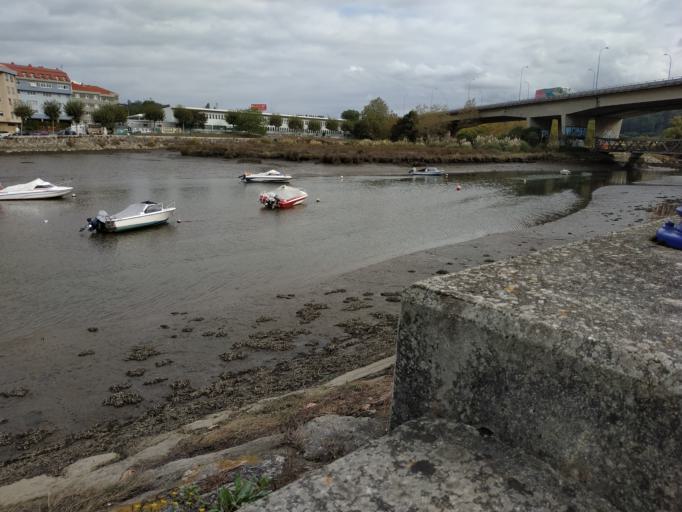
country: ES
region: Galicia
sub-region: Provincia da Coruna
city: Cambre
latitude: 43.3129
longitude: -8.3596
